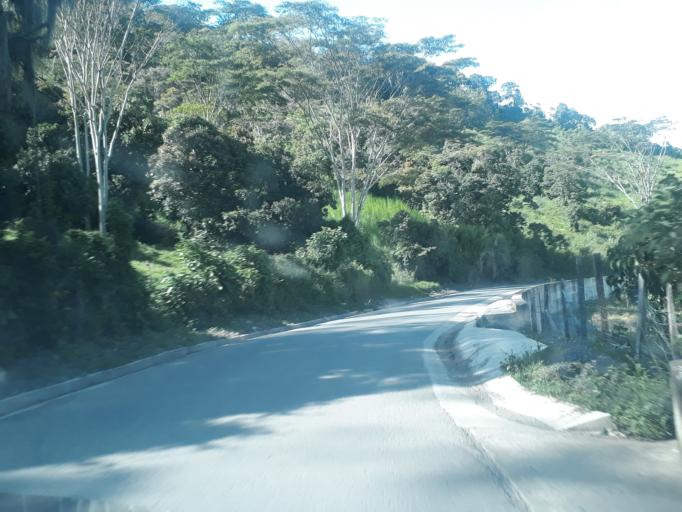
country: CO
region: Santander
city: Velez
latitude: 6.0283
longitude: -73.6554
